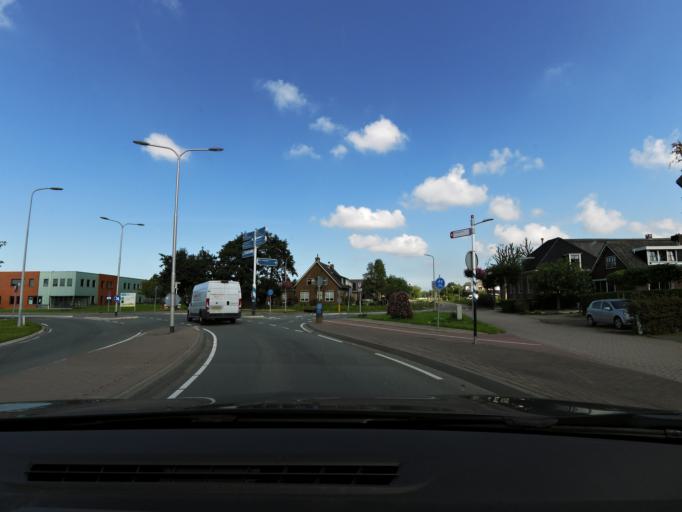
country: NL
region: North Holland
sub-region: Gemeente Aalsmeer
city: Aalsmeer
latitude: 52.2293
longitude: 4.7846
